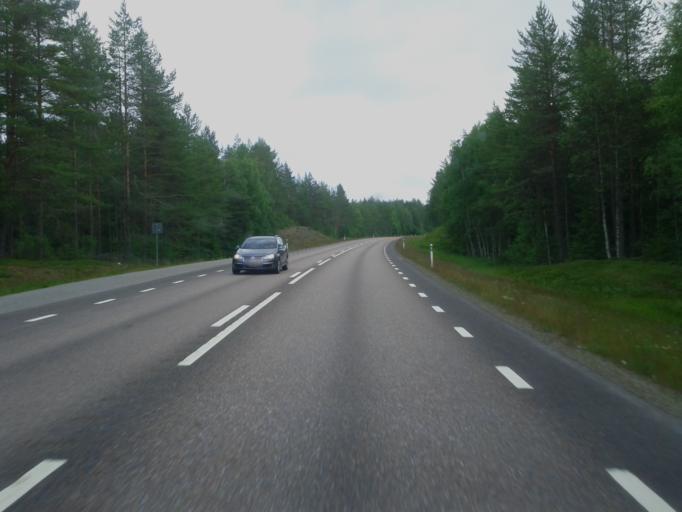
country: SE
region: Vaesterbotten
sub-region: Skelleftea Kommun
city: Burea
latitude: 64.3320
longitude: 21.2051
